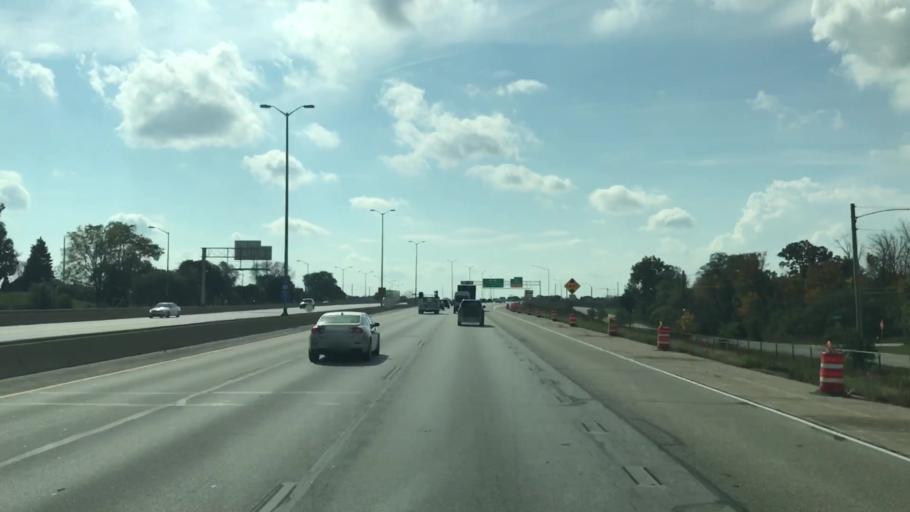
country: US
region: Wisconsin
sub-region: Waukesha County
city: Butler
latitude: 43.1417
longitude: -88.0551
